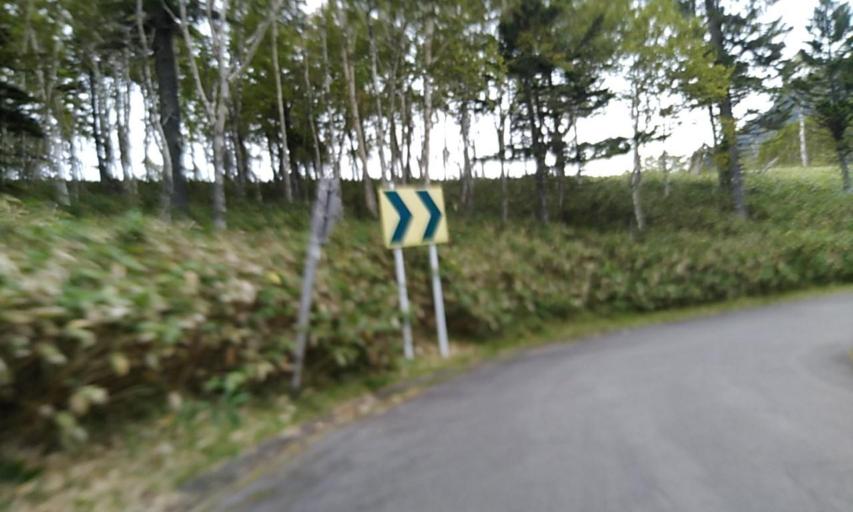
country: JP
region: Hokkaido
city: Bihoro
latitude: 43.5665
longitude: 144.2255
